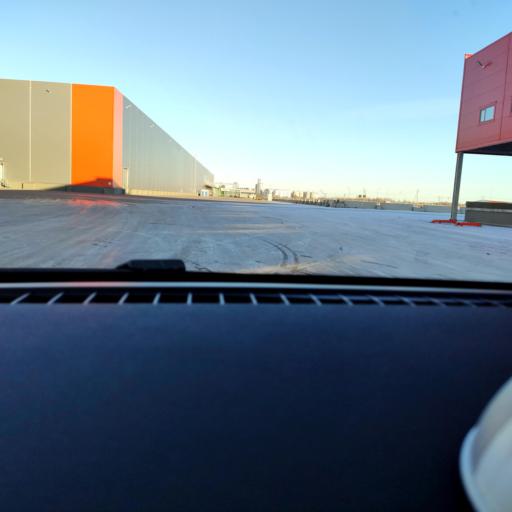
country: RU
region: Samara
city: Samara
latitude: 53.0910
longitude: 50.1281
